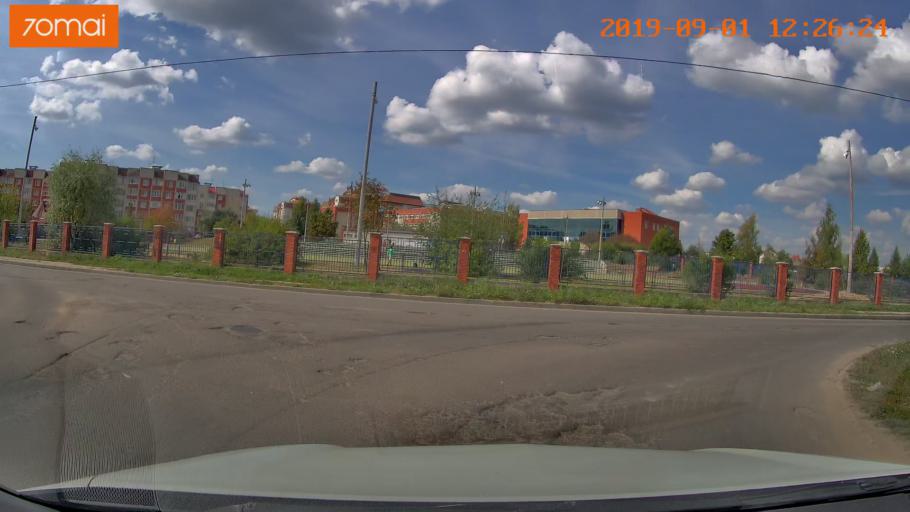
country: RU
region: Kaluga
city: Maloyaroslavets
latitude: 55.0017
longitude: 36.4615
